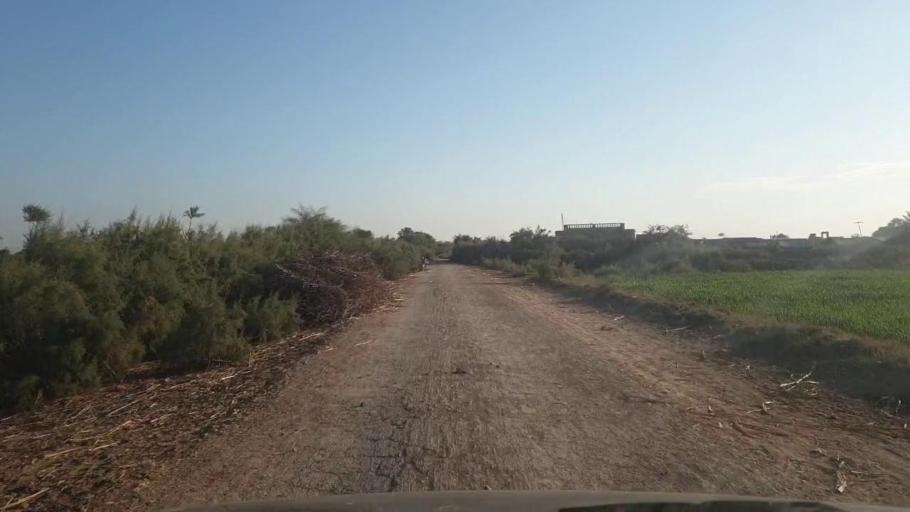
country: PK
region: Sindh
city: Sinjhoro
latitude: 26.0478
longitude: 68.8692
